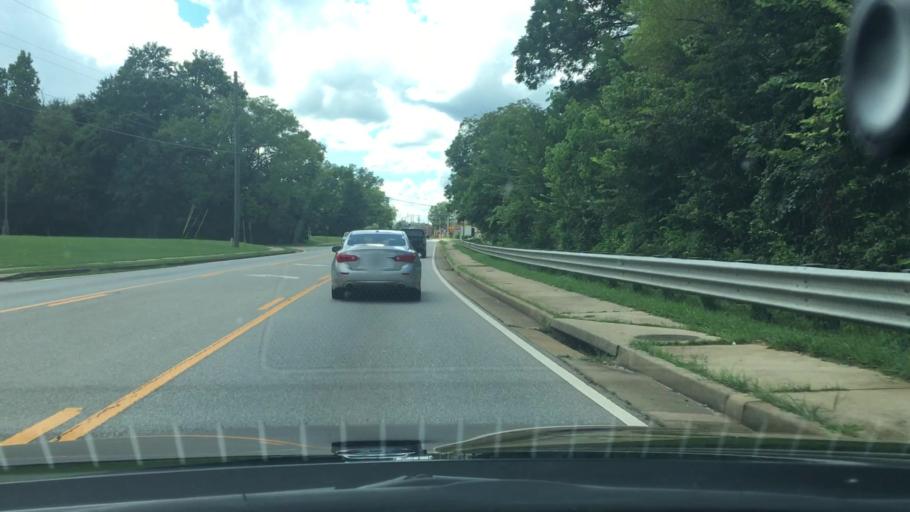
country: US
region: Georgia
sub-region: Putnam County
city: Eatonton
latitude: 33.3279
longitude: -83.3809
